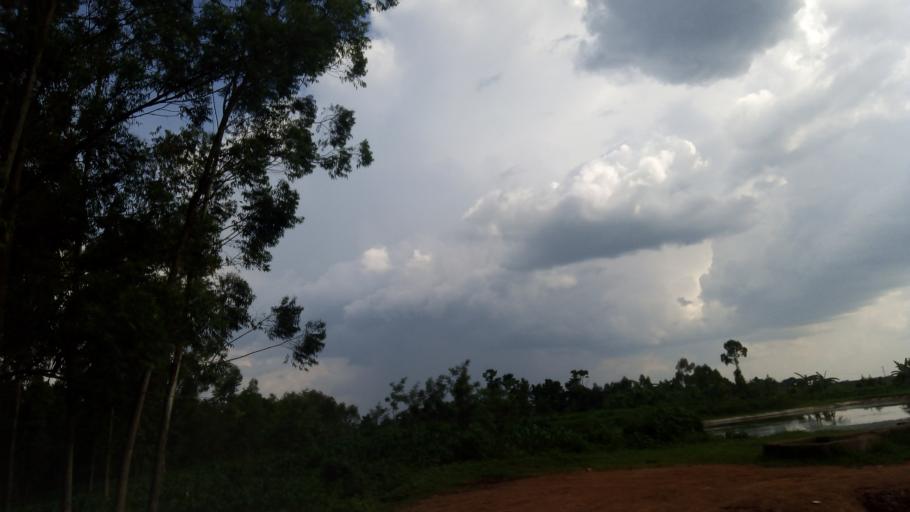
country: UG
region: Eastern Region
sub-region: Mbale District
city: Mbale
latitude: 1.0738
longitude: 34.1512
